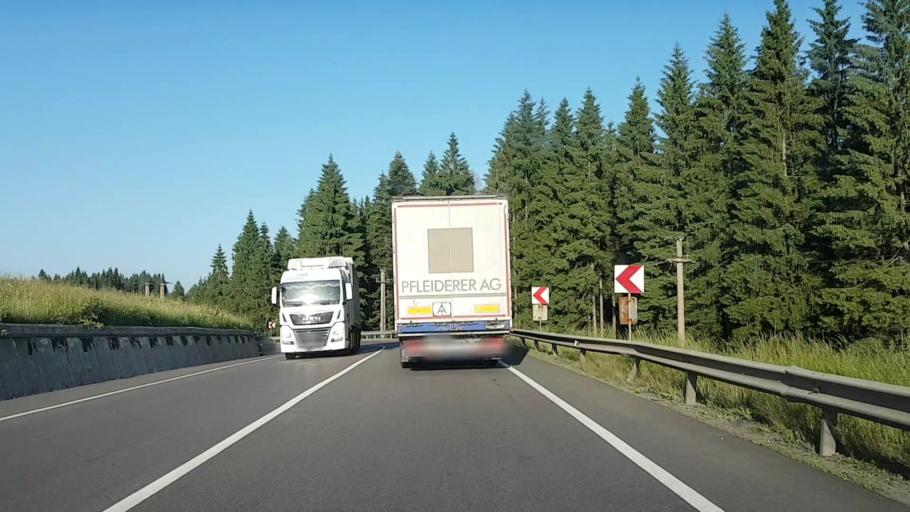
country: RO
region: Suceava
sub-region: Comuna Poiana Stampei
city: Poiana Stampei
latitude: 47.2859
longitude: 25.0609
